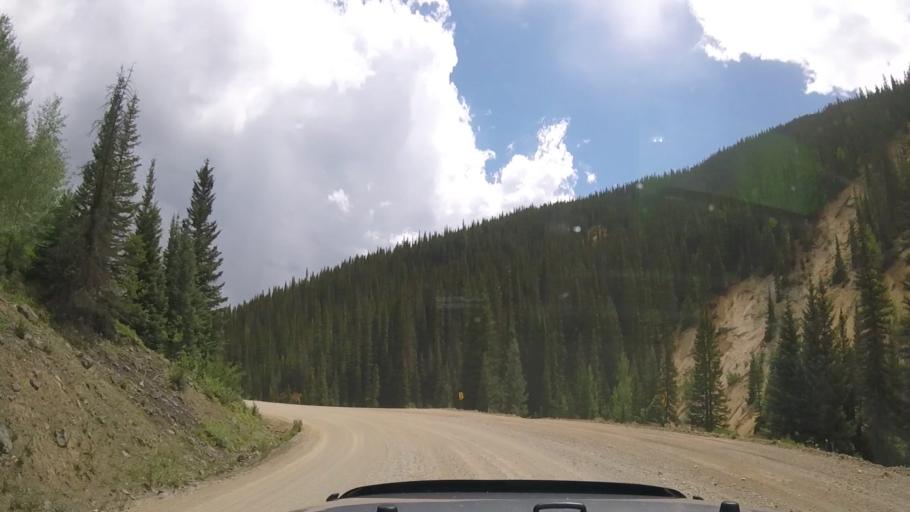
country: US
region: Colorado
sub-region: San Juan County
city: Silverton
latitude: 37.8356
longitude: -107.6774
